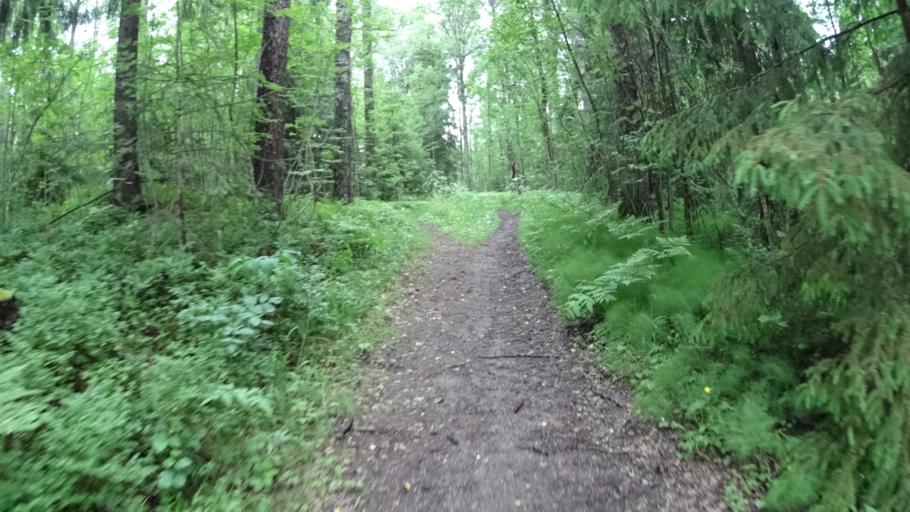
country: FI
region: Uusimaa
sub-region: Helsinki
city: Kilo
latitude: 60.2330
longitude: 24.7942
